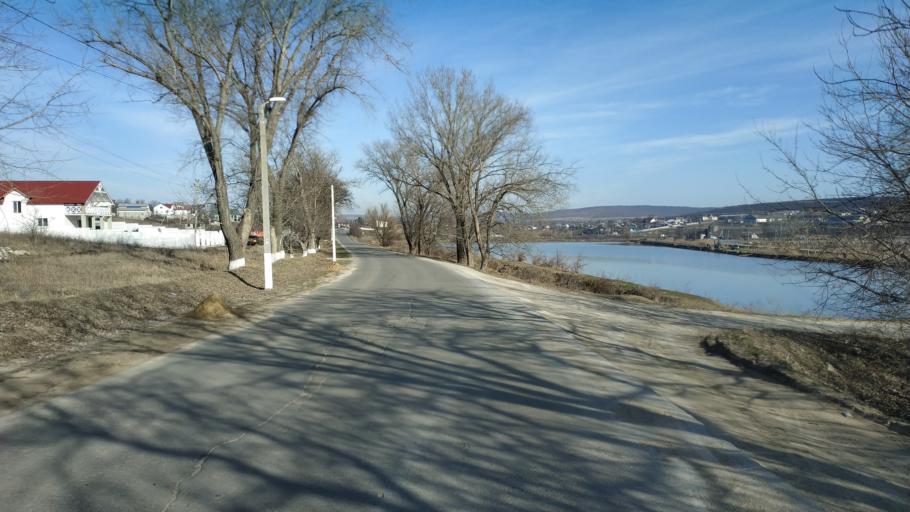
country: MD
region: Chisinau
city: Vatra
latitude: 46.9985
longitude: 28.6740
